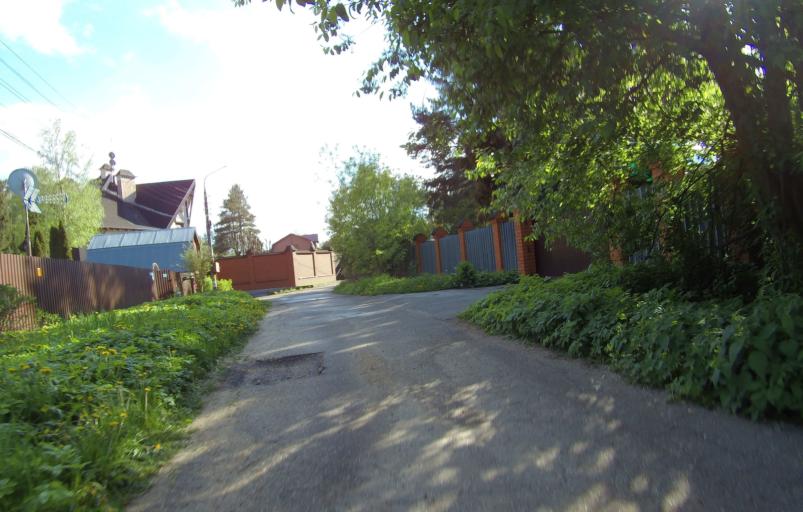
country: RU
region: Moskovskaya
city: Kratovo
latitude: 55.5918
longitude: 38.1718
